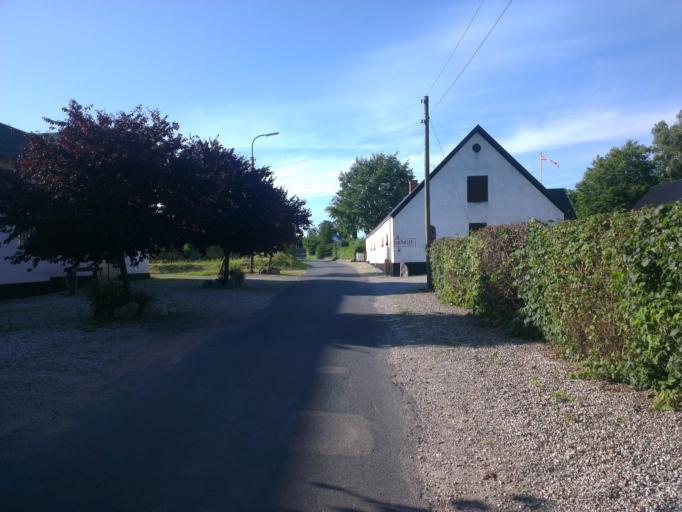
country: DK
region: Capital Region
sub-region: Frederikssund Kommune
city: Skibby
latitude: 55.7870
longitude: 11.9635
